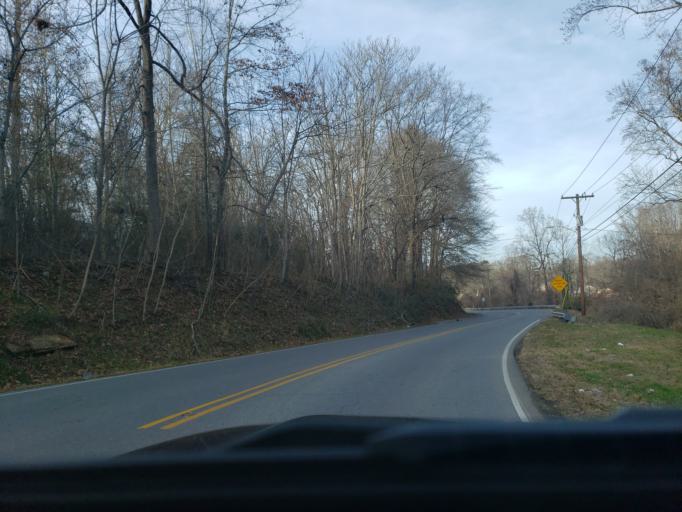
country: US
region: North Carolina
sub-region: Cleveland County
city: Shelby
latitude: 35.2807
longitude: -81.5246
